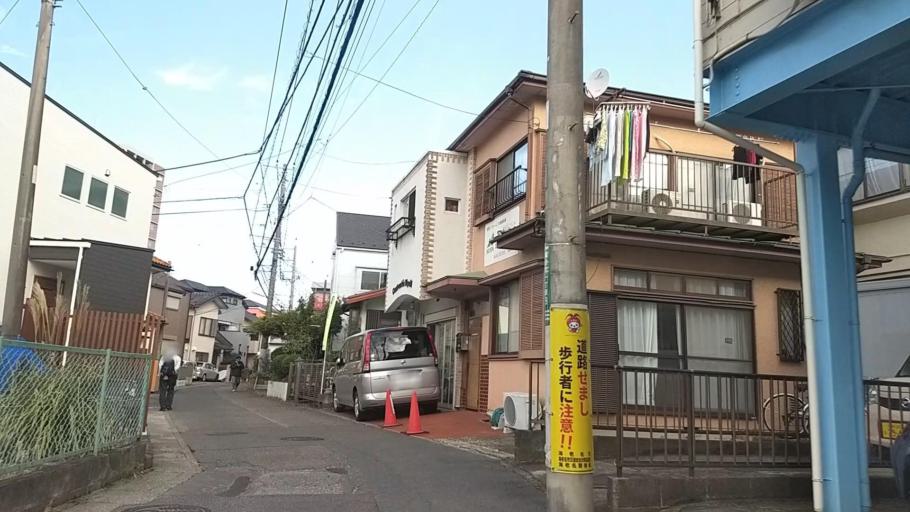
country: JP
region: Kanagawa
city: Zama
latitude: 35.4582
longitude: 139.3936
